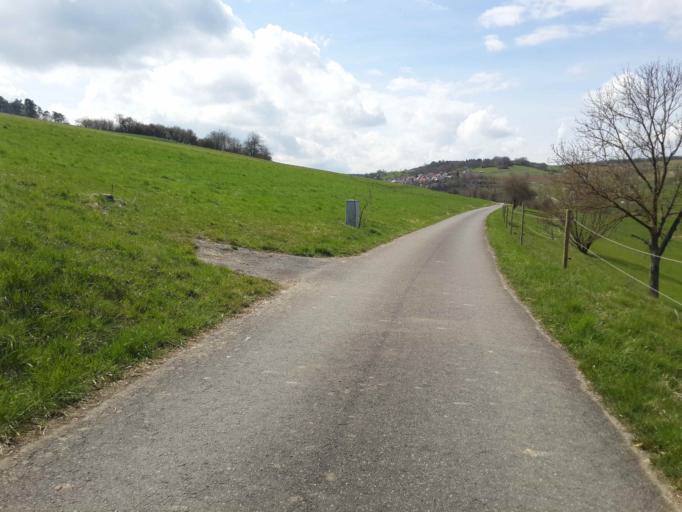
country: DE
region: Baden-Wuerttemberg
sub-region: Regierungsbezirk Stuttgart
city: Bad Mergentheim
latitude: 49.4515
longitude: 9.7634
